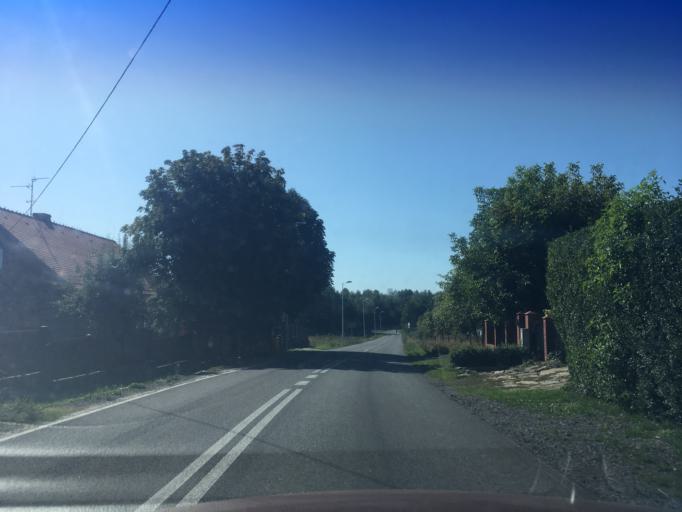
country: PL
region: Lower Silesian Voivodeship
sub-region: Powiat lubanski
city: Lesna
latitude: 50.9730
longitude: 15.2968
